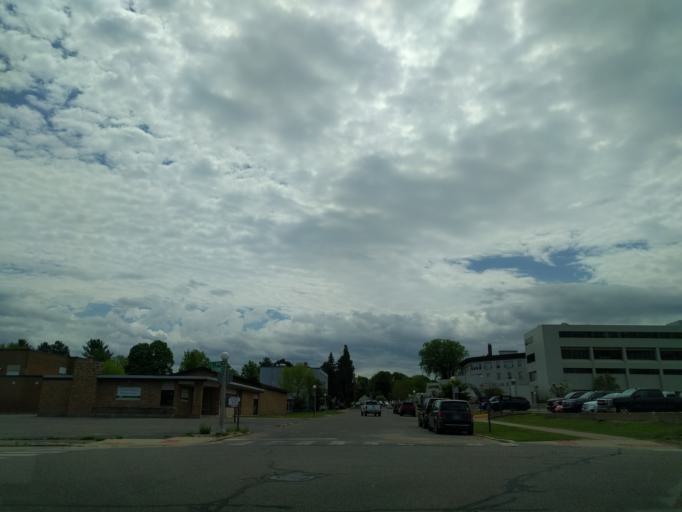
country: US
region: Michigan
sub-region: Marquette County
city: Marquette
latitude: 46.5557
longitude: -87.3986
